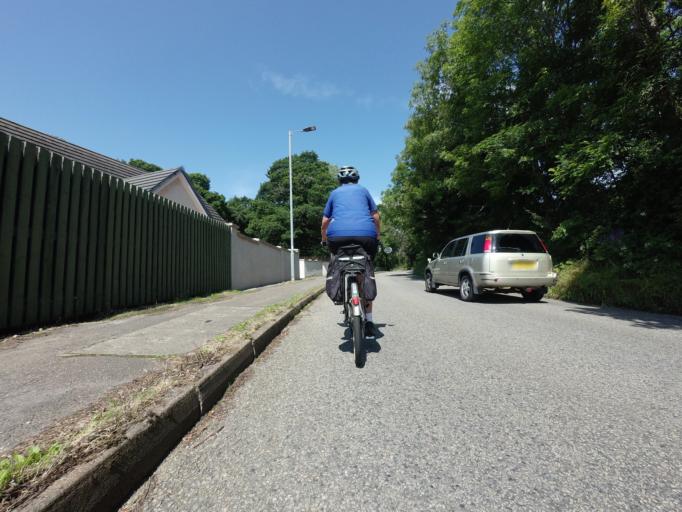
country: GB
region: Scotland
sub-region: Highland
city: Inverness
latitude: 57.5036
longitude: -4.2591
